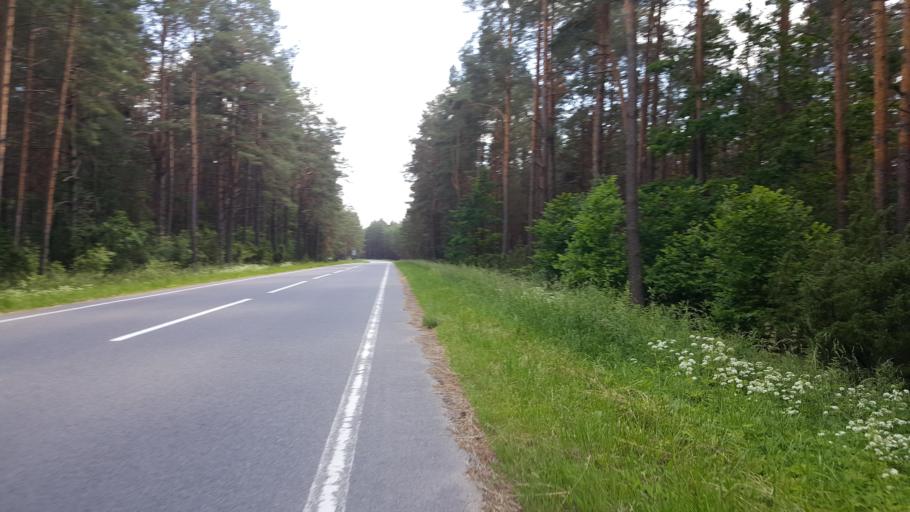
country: BY
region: Brest
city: Kamyanyuki
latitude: 52.5185
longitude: 23.6593
